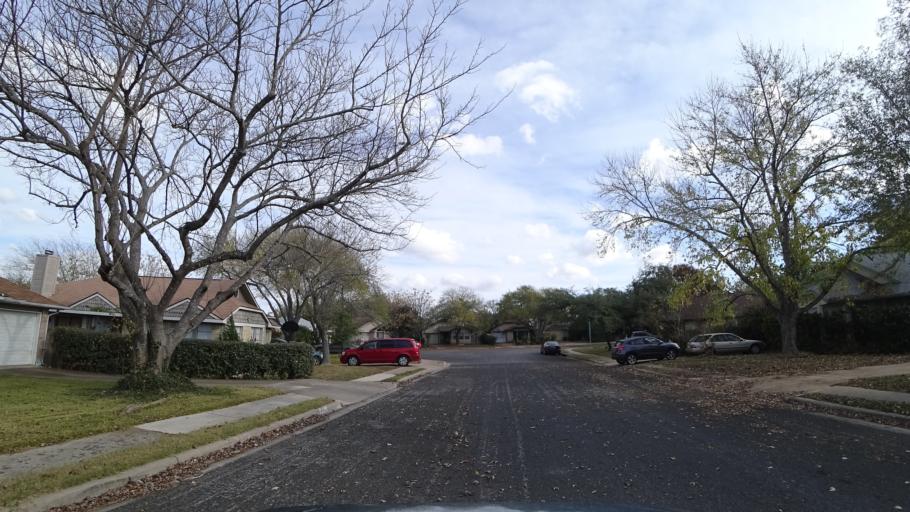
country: US
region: Texas
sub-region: Williamson County
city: Brushy Creek
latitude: 30.5097
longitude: -97.7382
